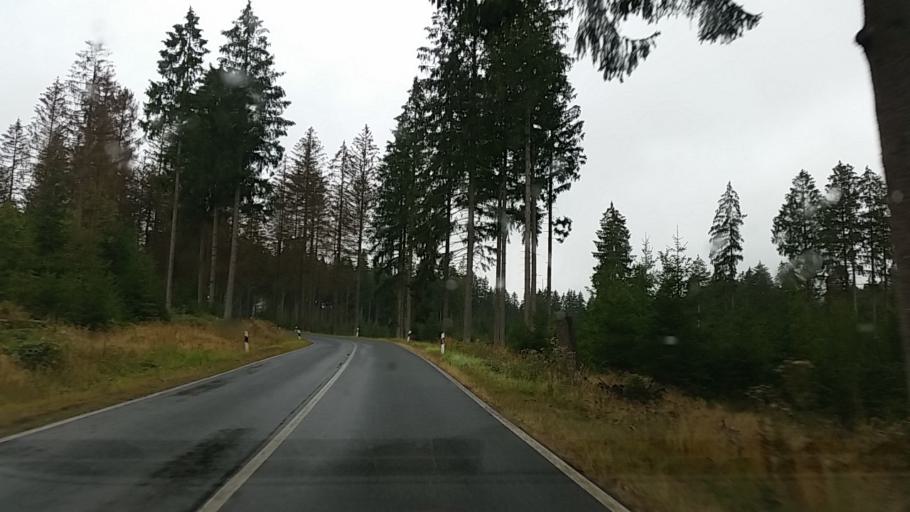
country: DE
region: Lower Saxony
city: Altenau
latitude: 51.7904
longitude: 10.4366
